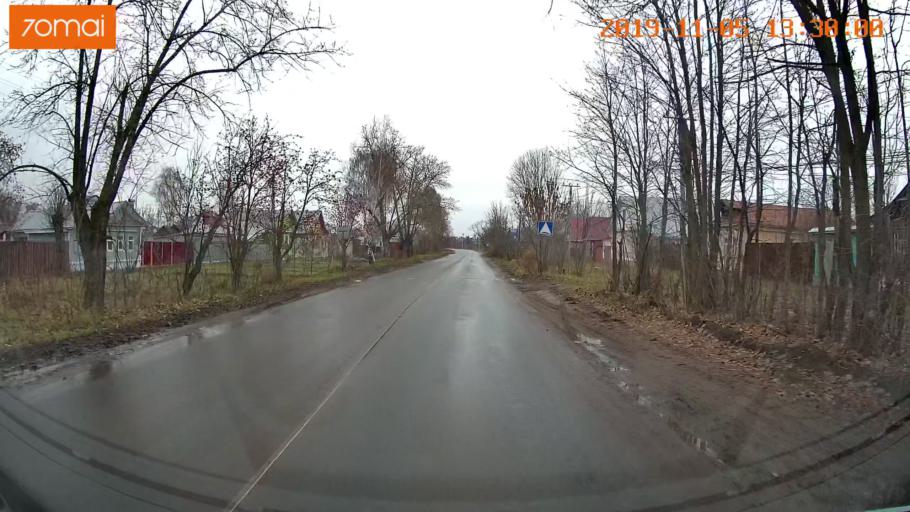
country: RU
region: Ivanovo
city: Shuya
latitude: 56.8641
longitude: 41.3969
